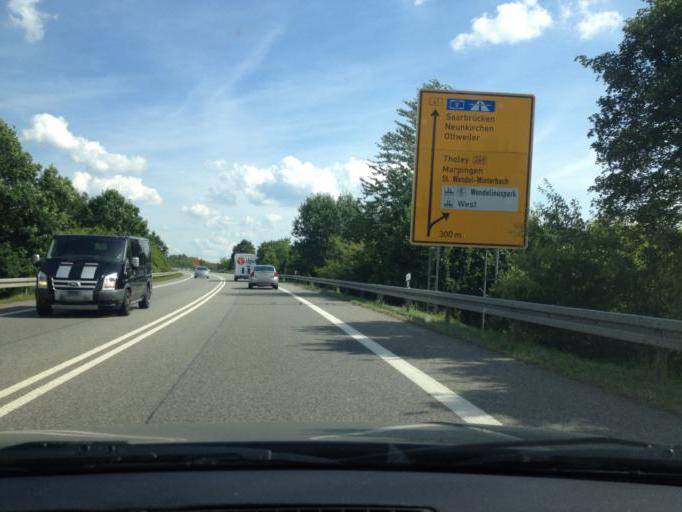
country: DE
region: Saarland
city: Sankt Wendel
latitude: 49.4756
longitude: 7.1454
